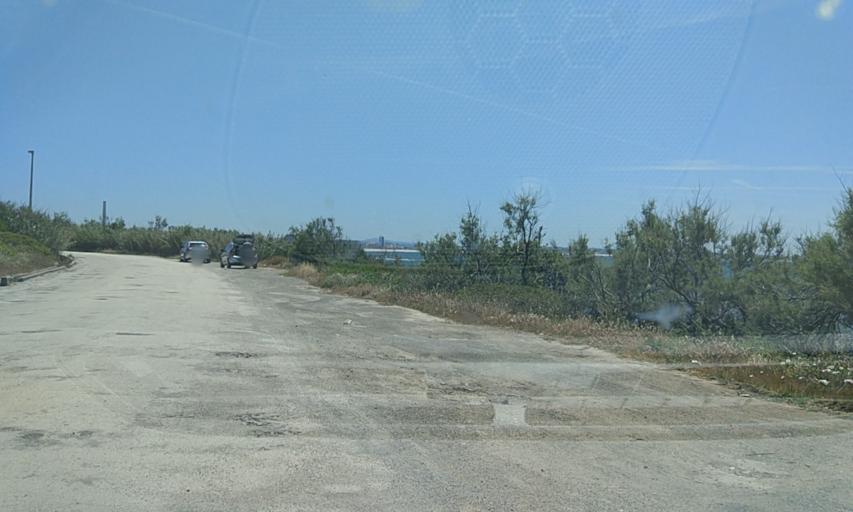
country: PT
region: Coimbra
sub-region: Figueira da Foz
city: Buarcos
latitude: 40.1786
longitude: -8.9054
